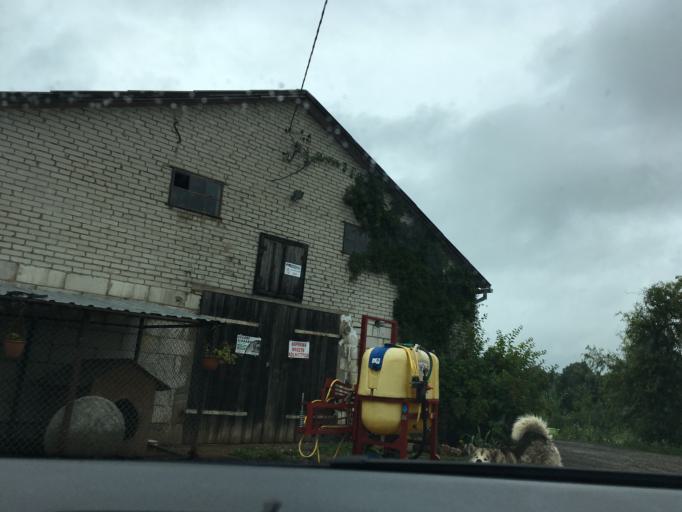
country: PL
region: Podlasie
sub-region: Powiat sejnenski
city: Krasnopol
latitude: 54.0926
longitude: 23.2657
